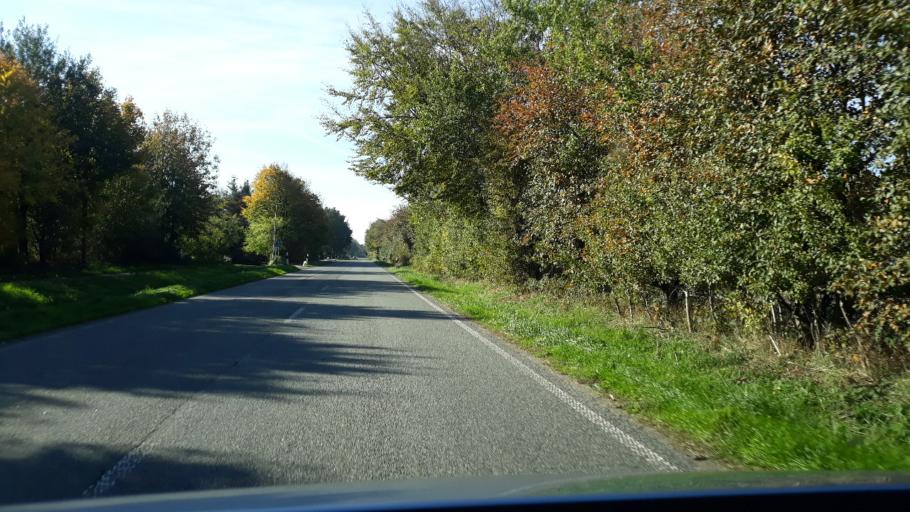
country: DE
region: Schleswig-Holstein
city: Borm
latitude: 54.4237
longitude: 9.4041
